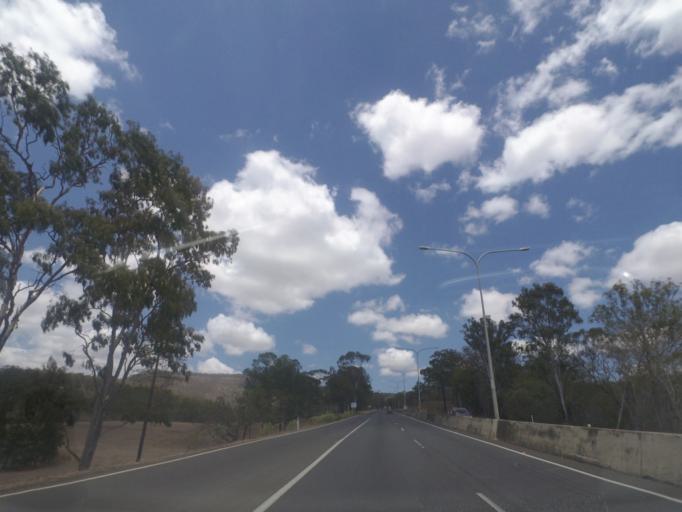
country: AU
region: Queensland
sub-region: Toowoomba
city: East Toowoomba
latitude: -27.5628
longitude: 152.0040
